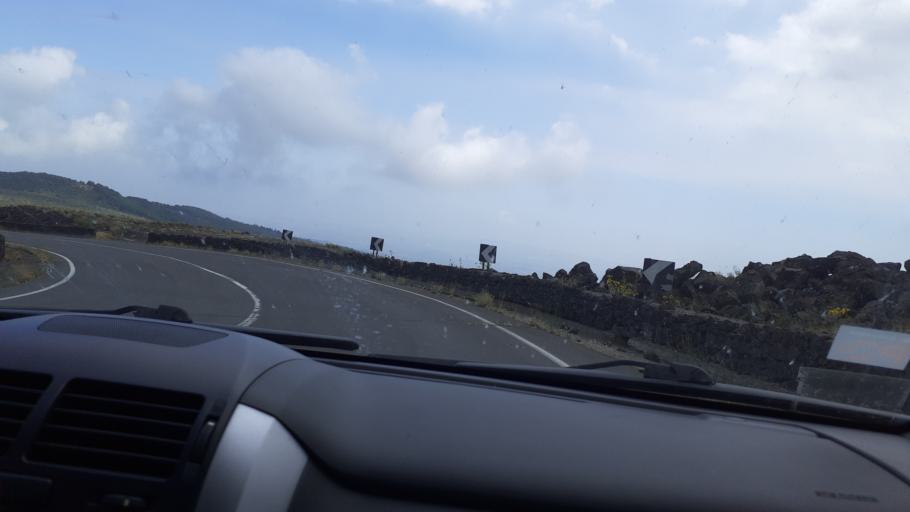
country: IT
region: Sicily
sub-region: Catania
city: Nicolosi
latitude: 37.6861
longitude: 15.0173
